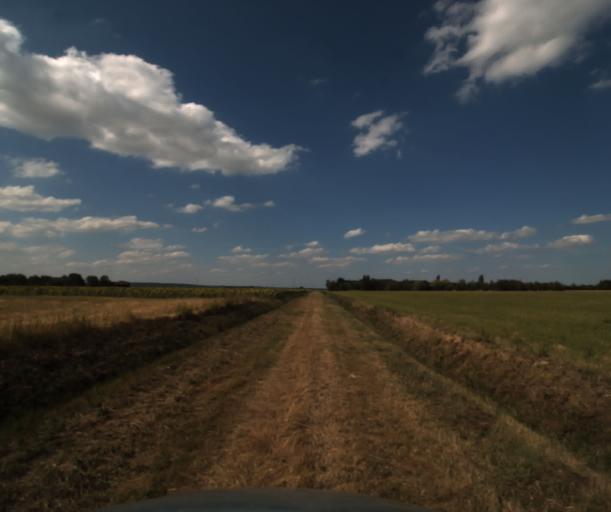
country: FR
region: Midi-Pyrenees
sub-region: Departement de la Haute-Garonne
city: Saint-Lys
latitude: 43.5265
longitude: 1.1787
